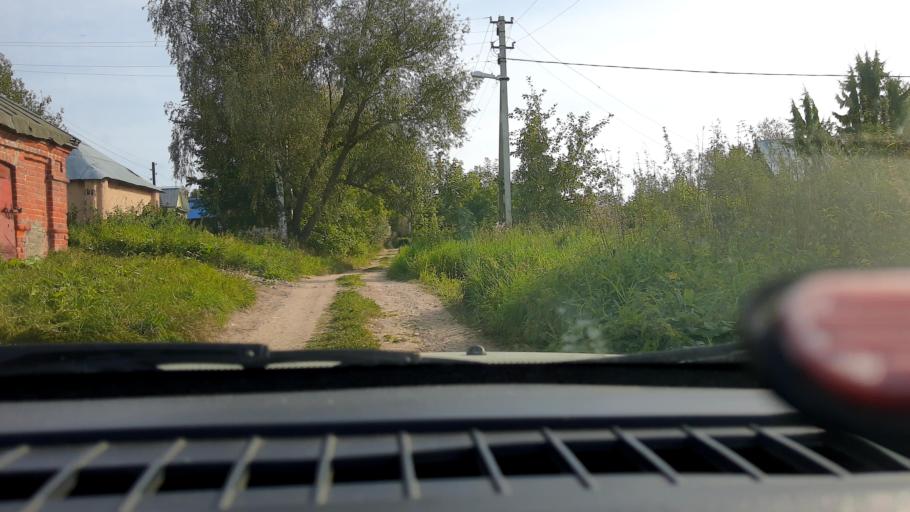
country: RU
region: Nizjnij Novgorod
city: Kstovo
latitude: 55.9963
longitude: 44.2273
